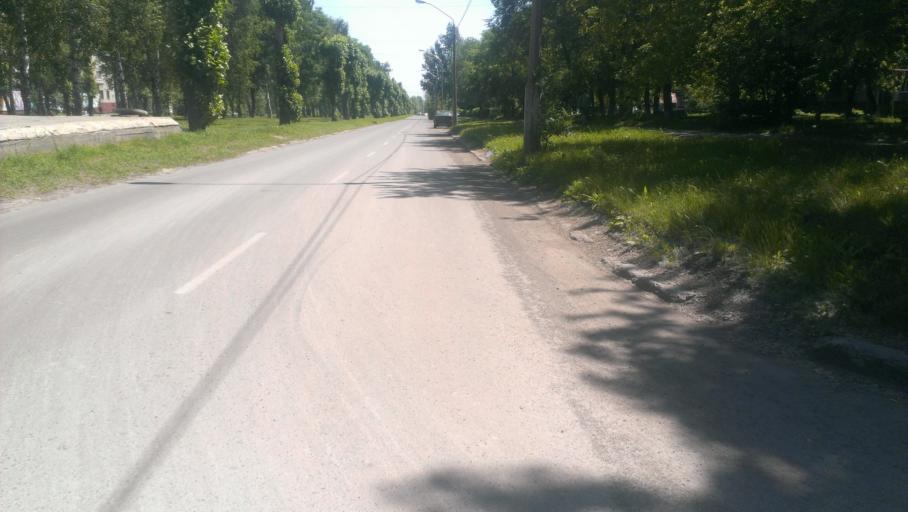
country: RU
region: Altai Krai
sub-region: Gorod Barnaulskiy
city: Barnaul
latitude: 53.3625
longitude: 83.7079
